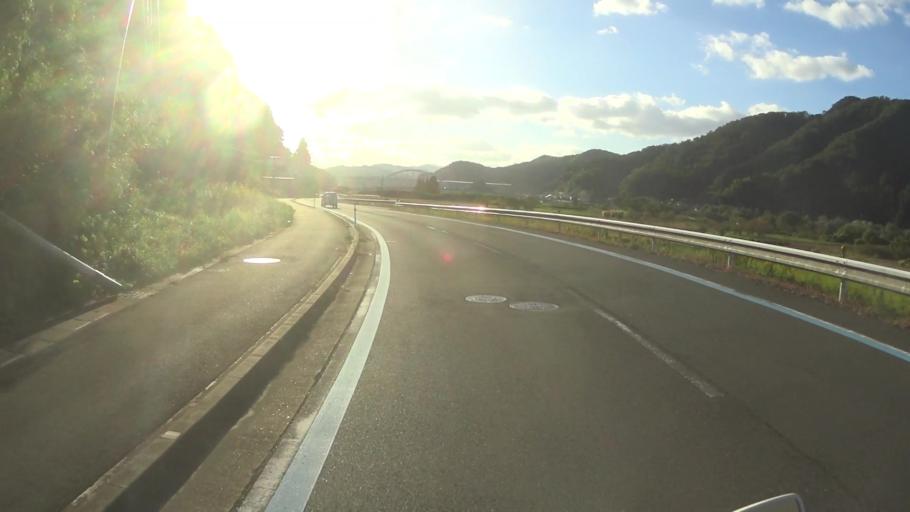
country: JP
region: Kyoto
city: Maizuru
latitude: 35.4263
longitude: 135.2267
